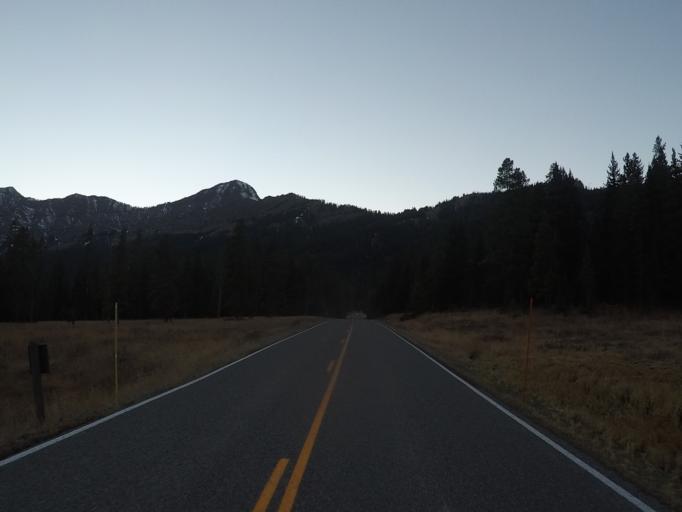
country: US
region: Montana
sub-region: Stillwater County
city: Absarokee
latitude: 45.0046
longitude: -110.0341
